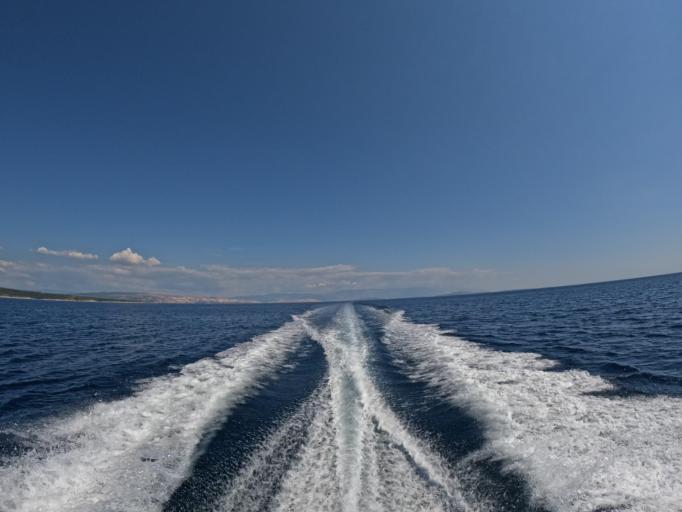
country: HR
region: Primorsko-Goranska
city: Cres
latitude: 44.9407
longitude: 14.4894
